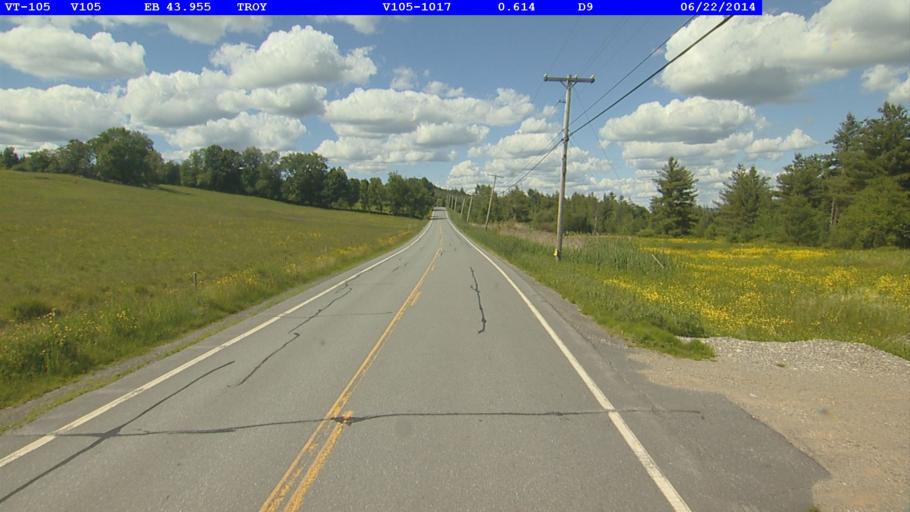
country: US
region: Vermont
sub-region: Orleans County
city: Newport
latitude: 44.9676
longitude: -72.4134
